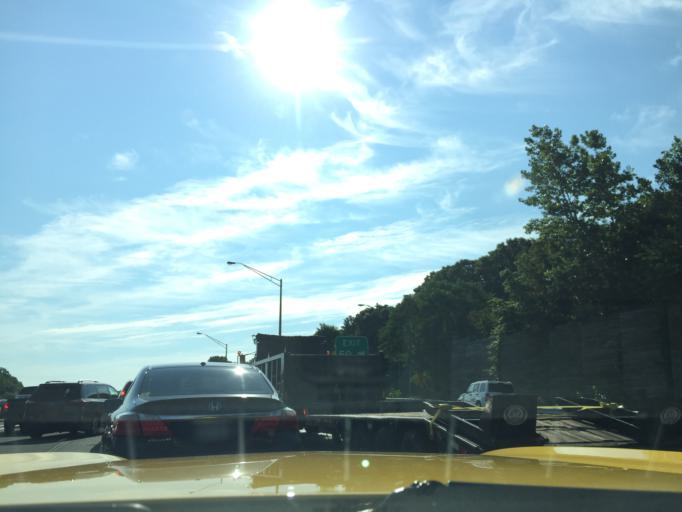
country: US
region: New York
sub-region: Suffolk County
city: Wheatley Heights
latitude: 40.7879
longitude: -73.3770
